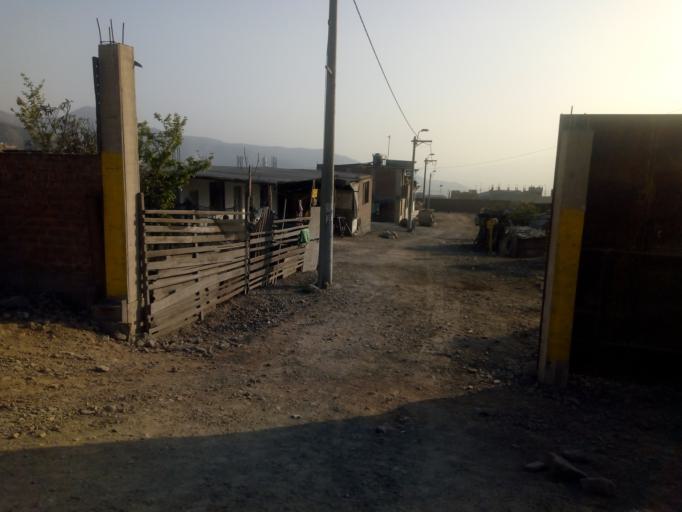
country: PE
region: Lima
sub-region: Lima
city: Urb. Santo Domingo
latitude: -11.9142
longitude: -76.9511
